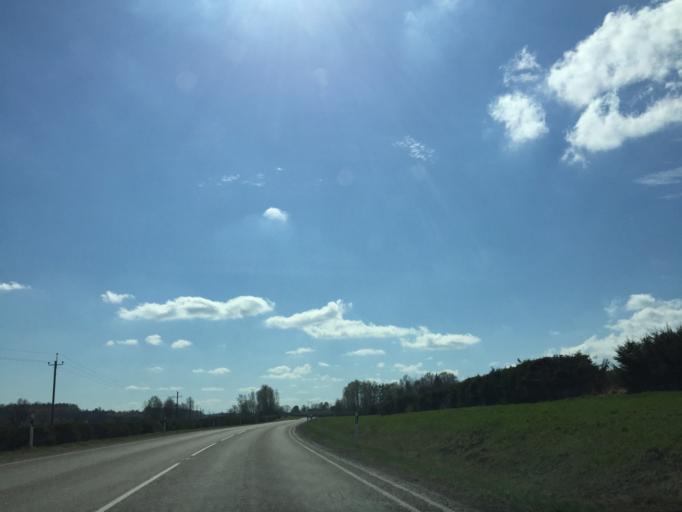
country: EE
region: Valgamaa
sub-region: Torva linn
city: Torva
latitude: 58.0451
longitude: 26.1919
